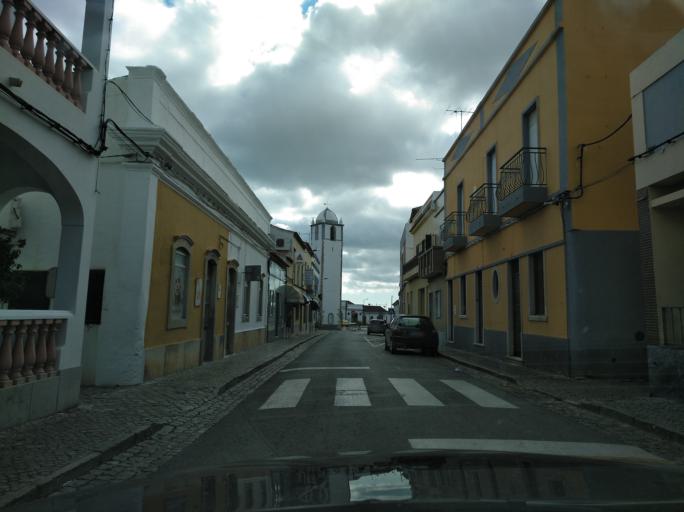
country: PT
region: Faro
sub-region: Tavira
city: Luz
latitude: 37.0927
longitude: -7.7040
